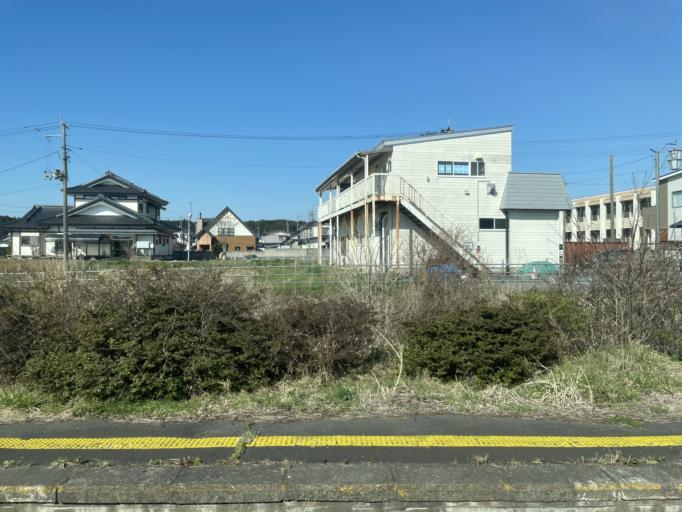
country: JP
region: Aomori
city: Hachinohe
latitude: 40.4101
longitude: 141.7152
